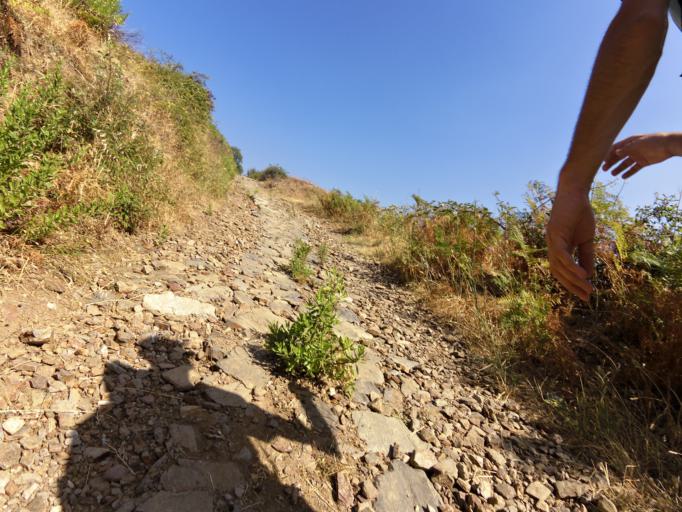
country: IT
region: Calabria
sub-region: Provincia di Reggio Calabria
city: Bivongi
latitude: 38.4985
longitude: 16.4538
